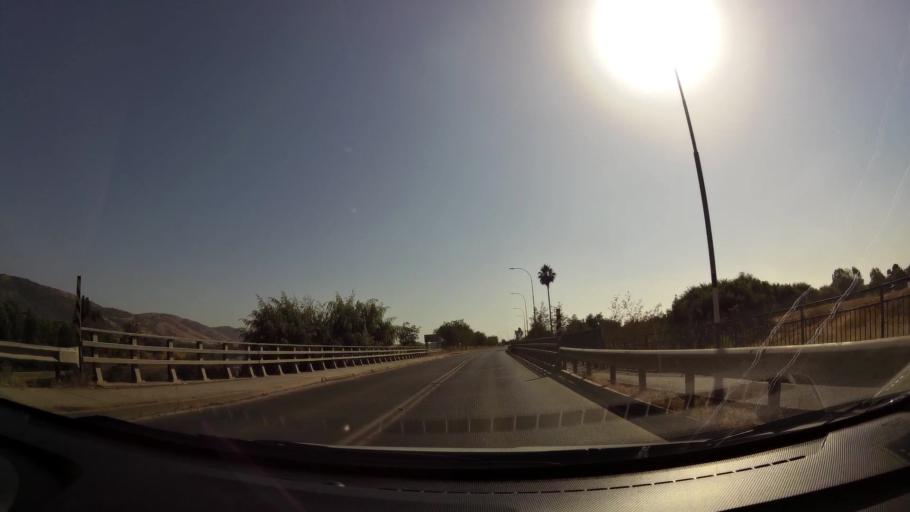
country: CL
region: Maule
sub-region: Provincia de Talca
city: Talca
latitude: -35.4022
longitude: -71.6611
